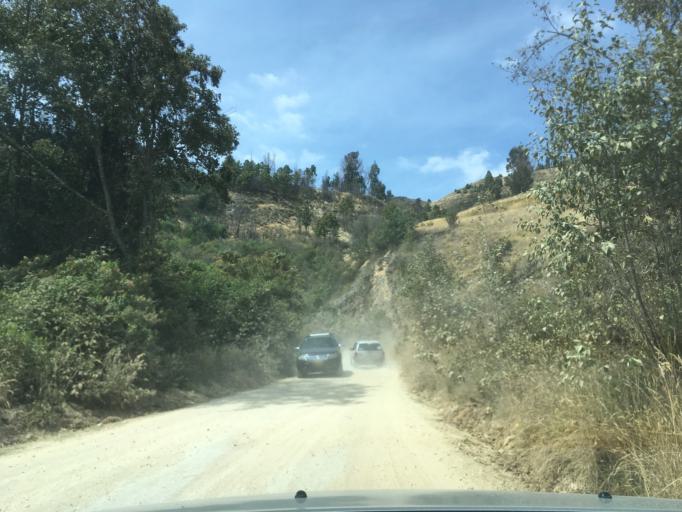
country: CO
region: Boyaca
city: Aquitania
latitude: 5.5873
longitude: -72.9222
